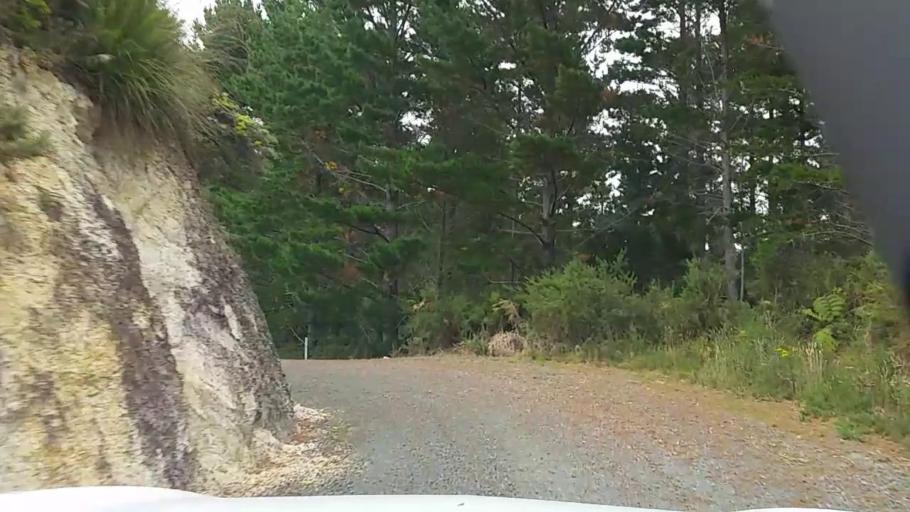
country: NZ
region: Northland
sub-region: Far North District
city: Kawakawa
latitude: -35.4618
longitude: 174.2634
